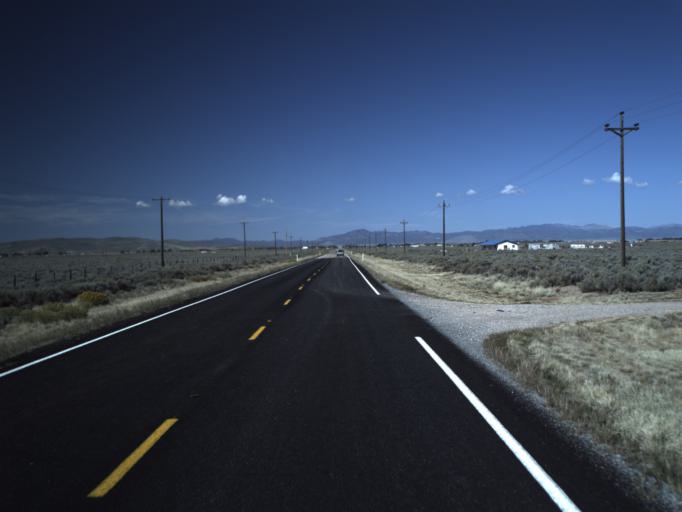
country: US
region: Utah
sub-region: Washington County
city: Enterprise
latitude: 37.6914
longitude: -113.6059
